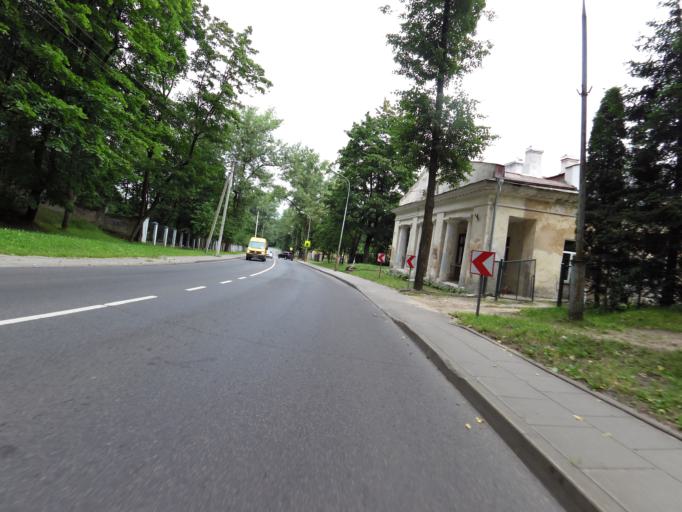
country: LT
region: Vilnius County
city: Rasos
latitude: 54.6662
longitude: 25.2985
